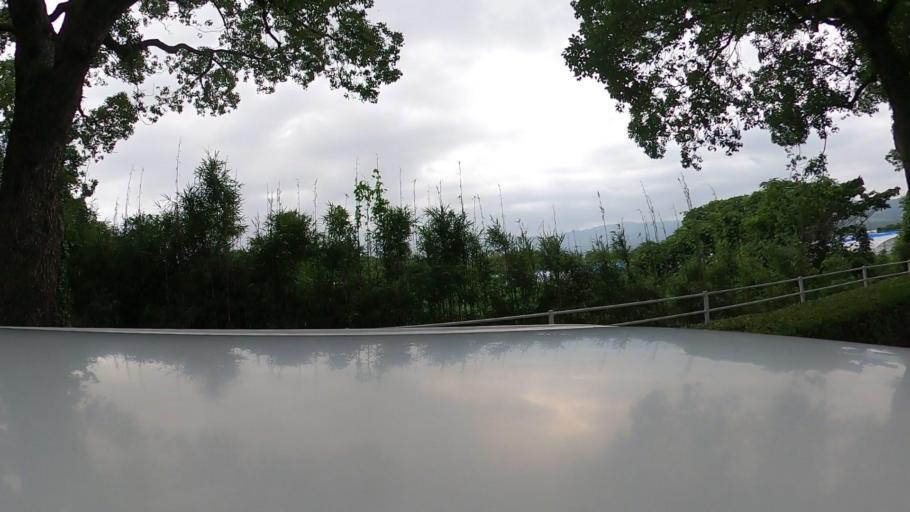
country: JP
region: Kumamoto
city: Ozu
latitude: 32.8308
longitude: 130.8571
